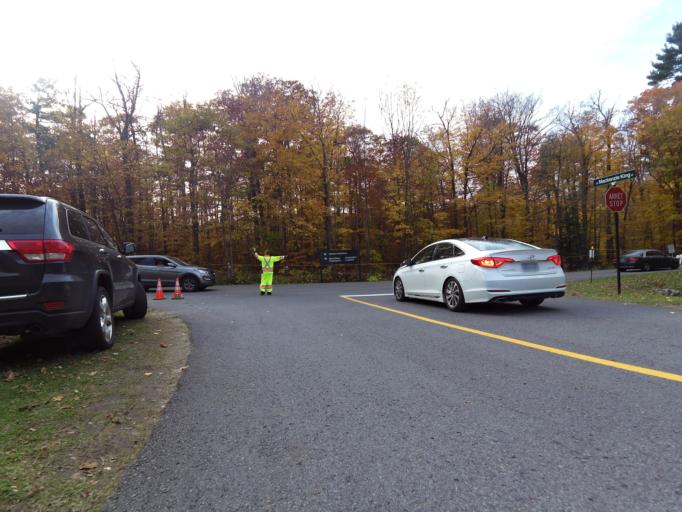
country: CA
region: Quebec
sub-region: Outaouais
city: Gatineau
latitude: 45.4781
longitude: -75.8459
